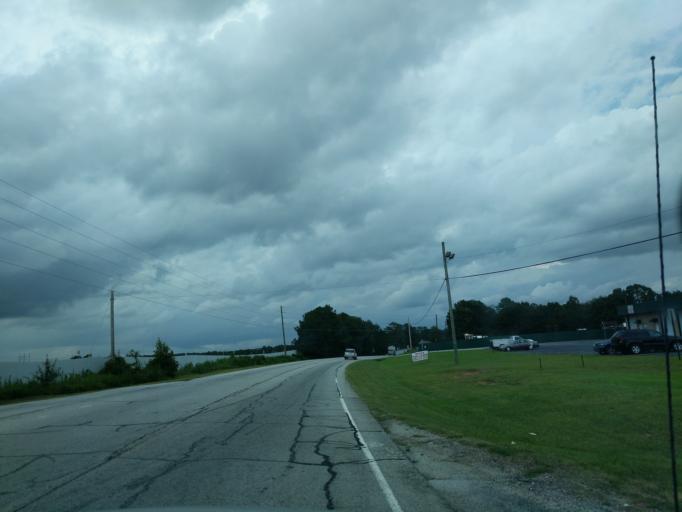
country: US
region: Georgia
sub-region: Walton County
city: Loganville
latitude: 33.8016
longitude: -83.9553
